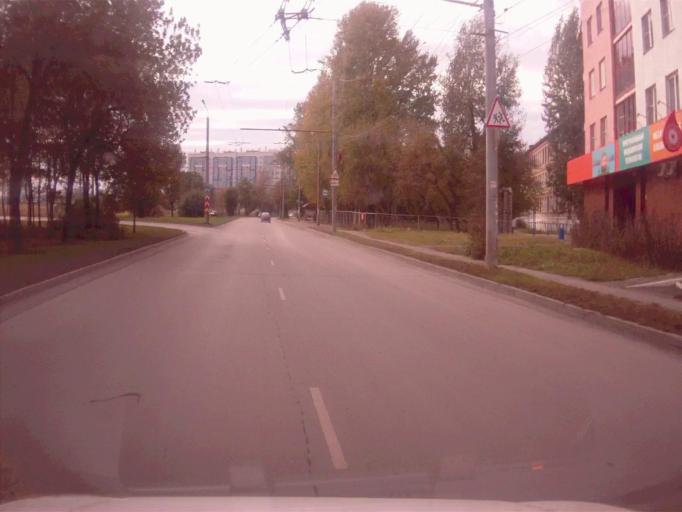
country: RU
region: Chelyabinsk
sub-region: Gorod Chelyabinsk
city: Chelyabinsk
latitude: 55.1170
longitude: 61.4356
